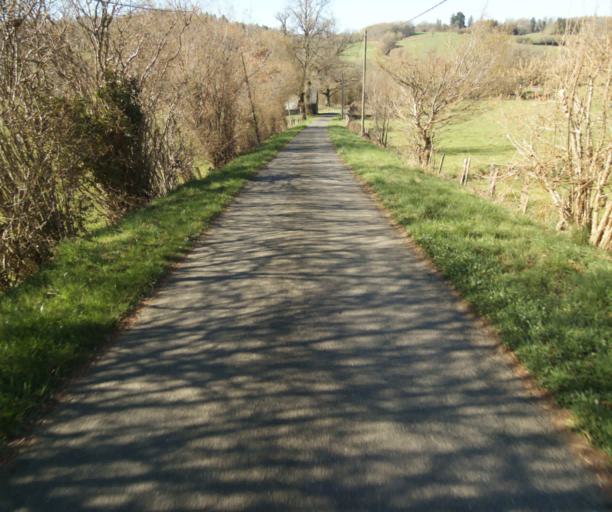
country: FR
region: Limousin
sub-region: Departement de la Correze
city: Chamboulive
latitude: 45.4191
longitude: 1.7085
